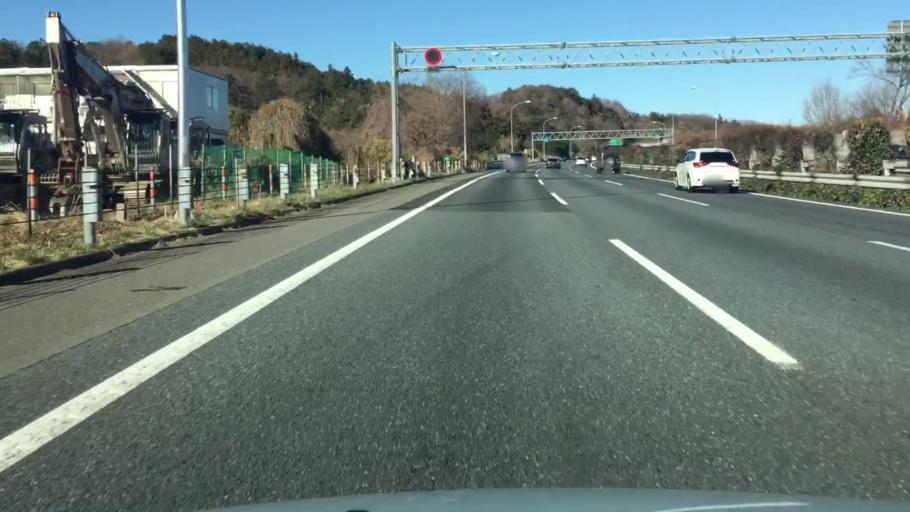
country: JP
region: Saitama
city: Ogawa
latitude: 36.0694
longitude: 139.3086
